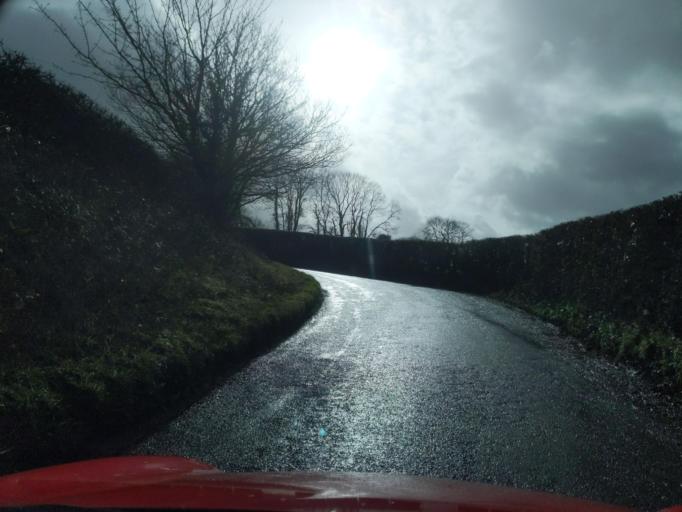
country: GB
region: England
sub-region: Devon
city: Ivybridge
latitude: 50.3842
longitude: -3.9352
